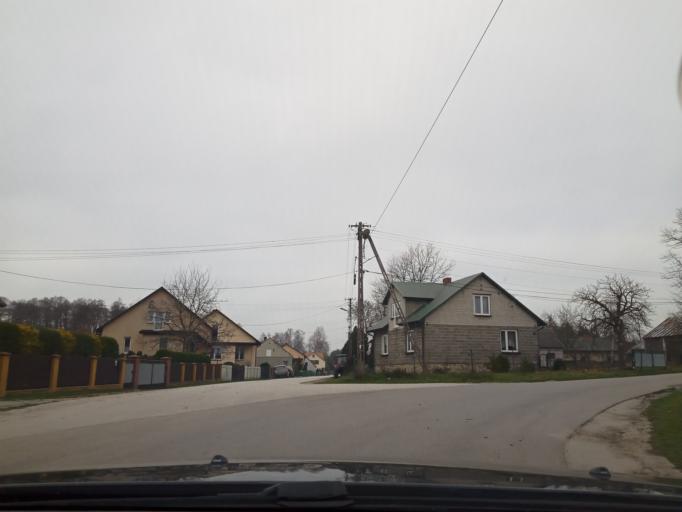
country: PL
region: Swietokrzyskie
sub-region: Powiat jedrzejowski
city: Imielno
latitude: 50.5886
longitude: 20.4758
